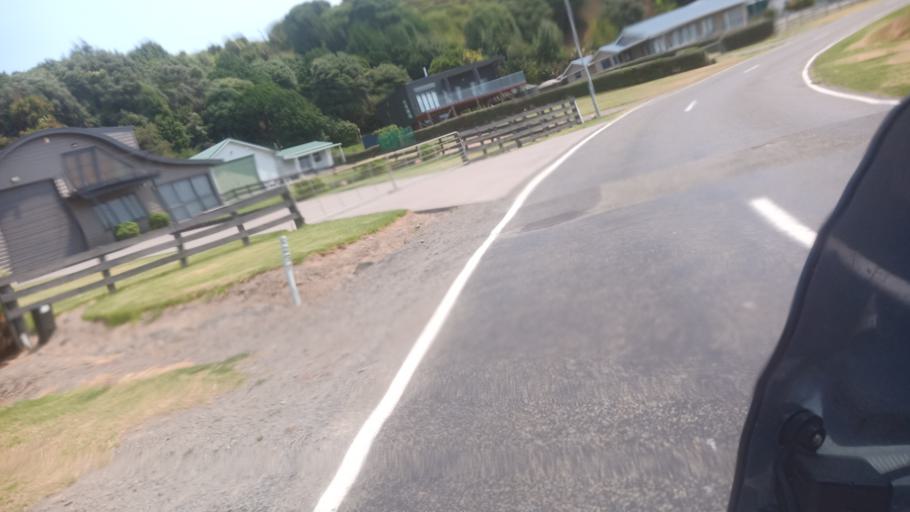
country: NZ
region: Bay of Plenty
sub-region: Opotiki District
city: Opotiki
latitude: -37.6171
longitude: 177.9090
